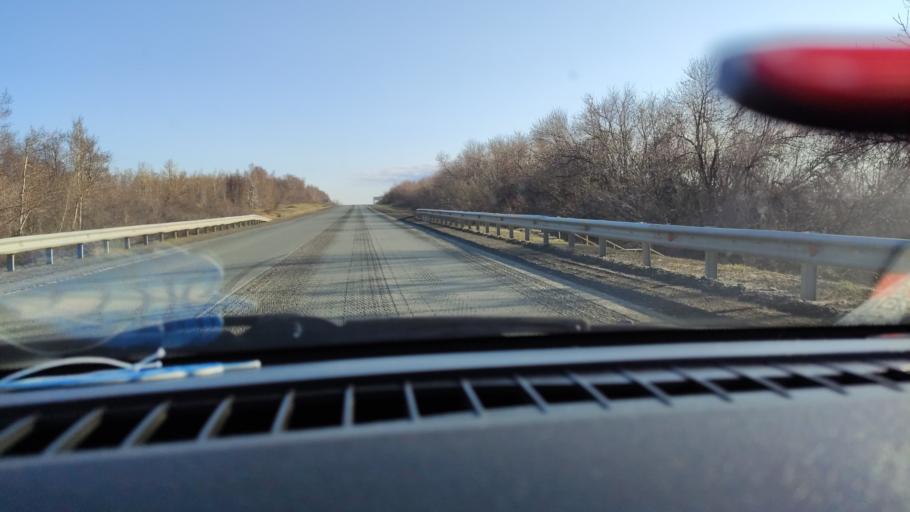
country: RU
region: Saratov
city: Dukhovnitskoye
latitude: 52.6330
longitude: 48.1856
